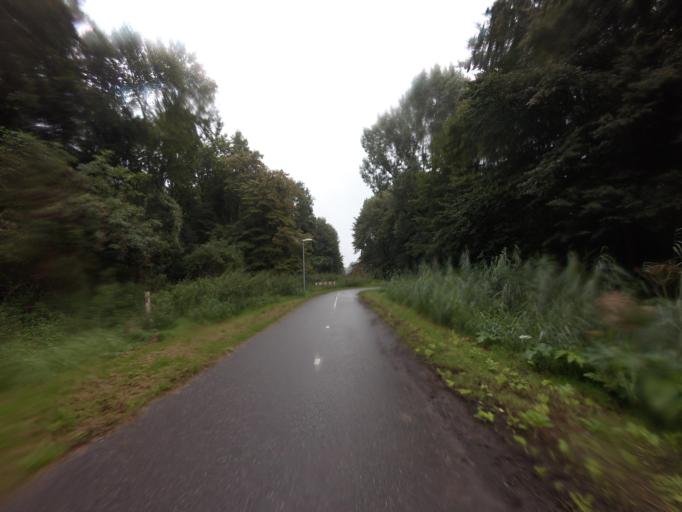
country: NL
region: North Holland
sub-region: Gemeente Huizen
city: Huizen
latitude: 52.3330
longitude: 5.2586
